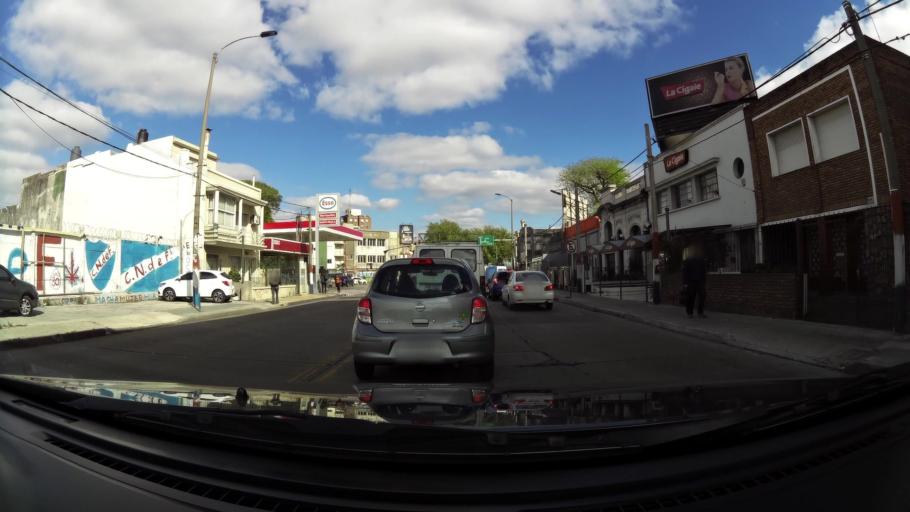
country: UY
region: Montevideo
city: Montevideo
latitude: -34.8853
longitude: -56.1652
